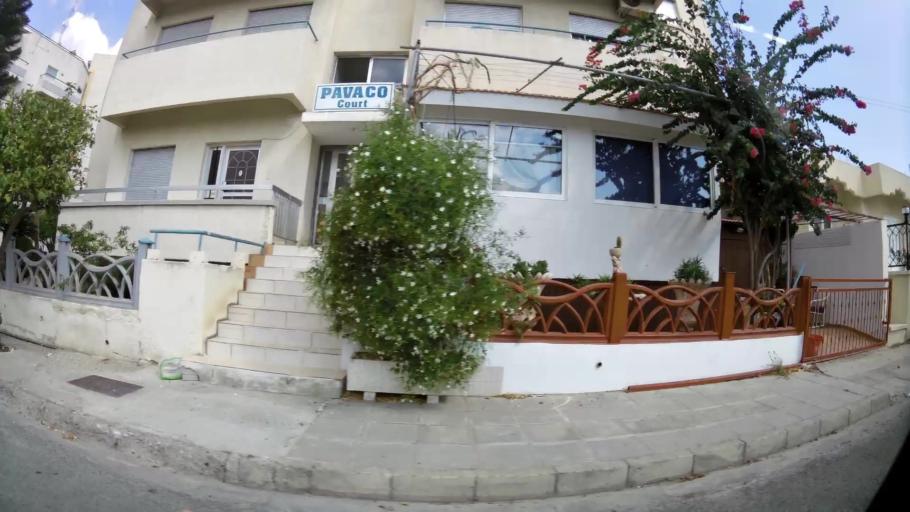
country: CY
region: Larnaka
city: Larnaca
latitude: 34.9191
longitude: 33.6154
